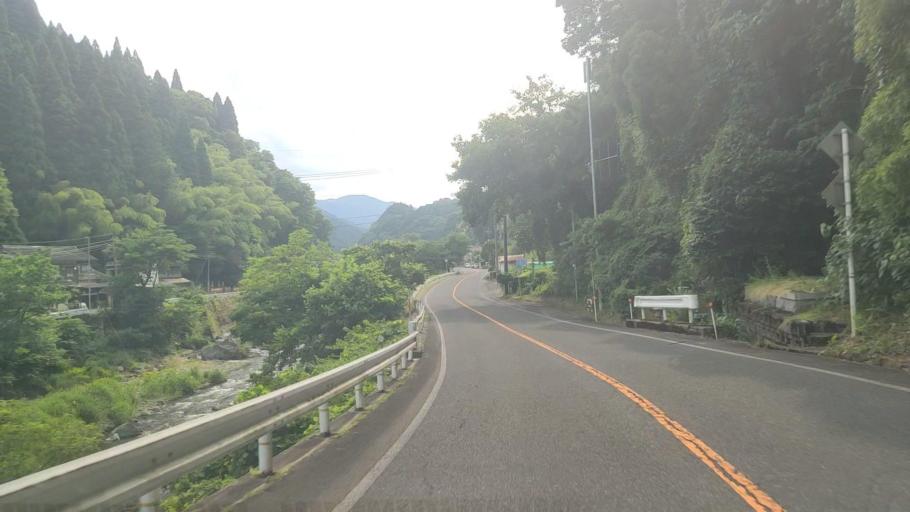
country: JP
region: Tottori
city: Tottori
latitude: 35.3337
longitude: 134.1284
